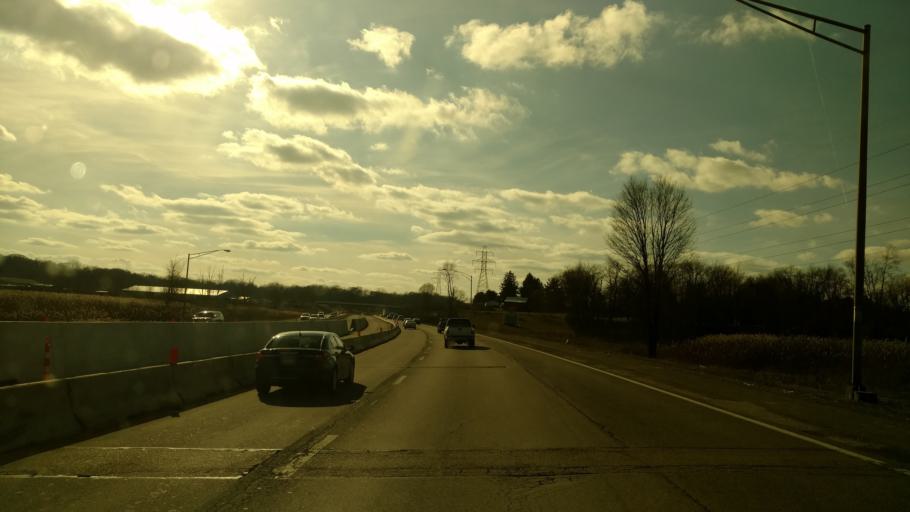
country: US
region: Ohio
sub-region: Summit County
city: Norton
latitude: 41.0408
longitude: -81.6130
